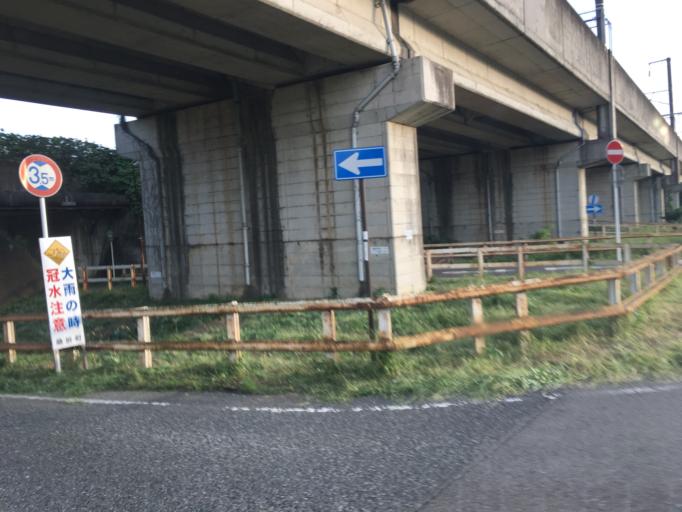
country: JP
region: Fukushima
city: Hobaramachi
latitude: 37.8523
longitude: 140.5147
